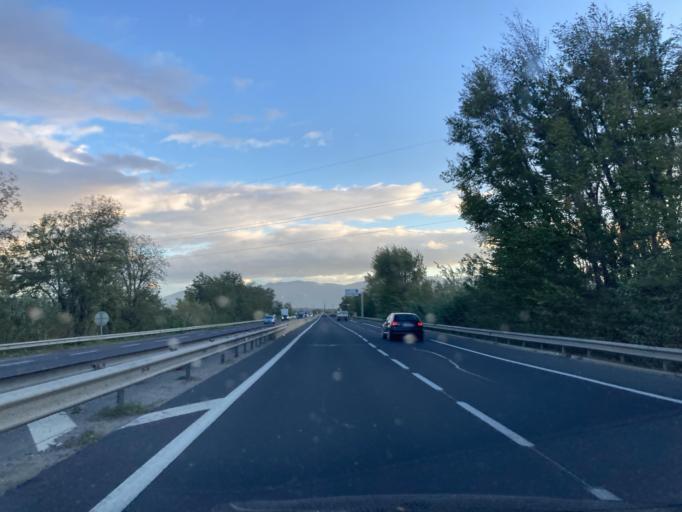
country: FR
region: Languedoc-Roussillon
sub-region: Departement des Pyrenees-Orientales
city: Villeneuve-de-la-Raho
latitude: 42.6522
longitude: 2.9270
